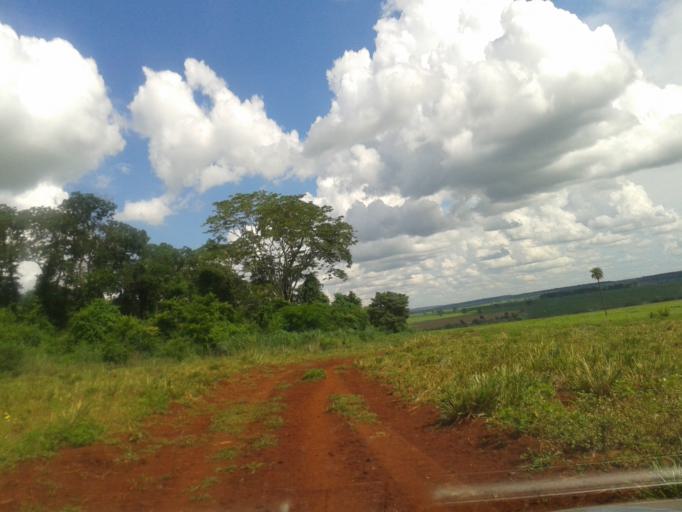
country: BR
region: Minas Gerais
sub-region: Capinopolis
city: Capinopolis
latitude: -18.7724
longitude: -49.8278
